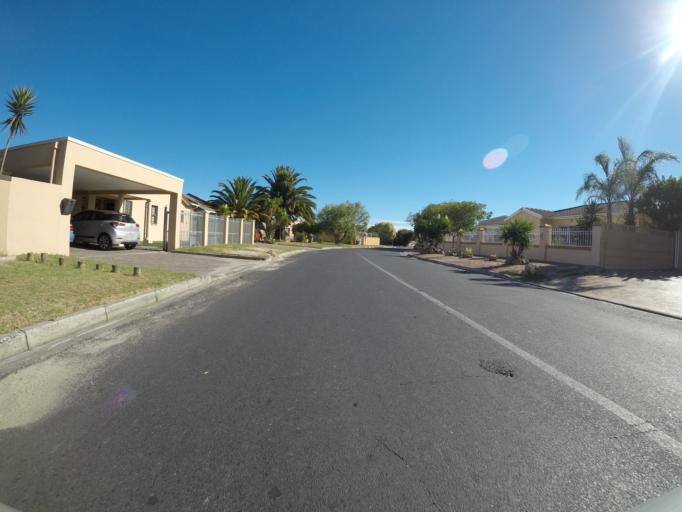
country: ZA
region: Western Cape
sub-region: City of Cape Town
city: Kraaifontein
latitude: -33.9442
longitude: 18.6831
